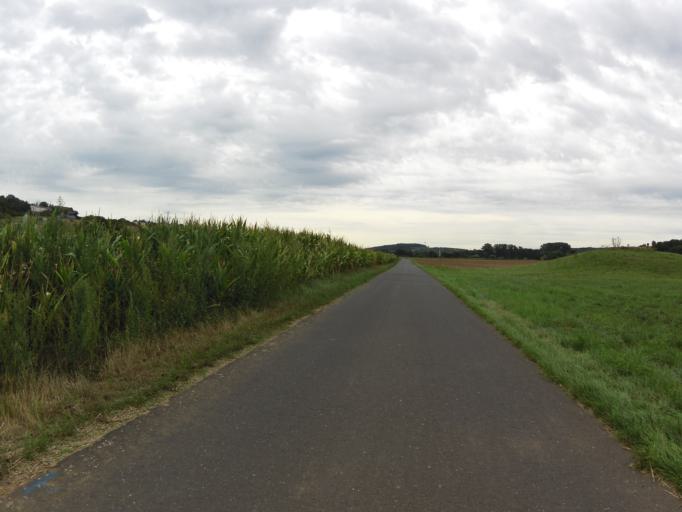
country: DE
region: Bavaria
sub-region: Regierungsbezirk Unterfranken
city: Gadheim
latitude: 50.0242
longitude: 10.3302
